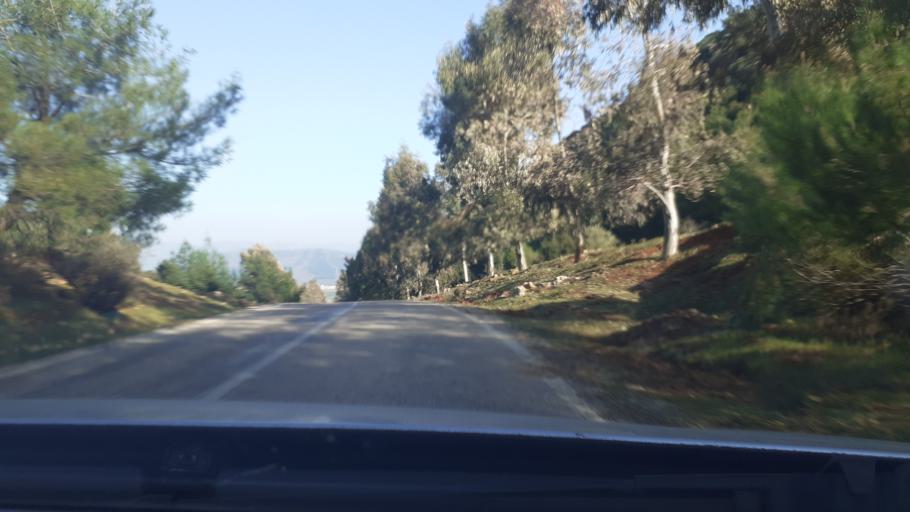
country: TR
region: Hatay
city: Aktepe
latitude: 36.7330
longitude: 36.4728
